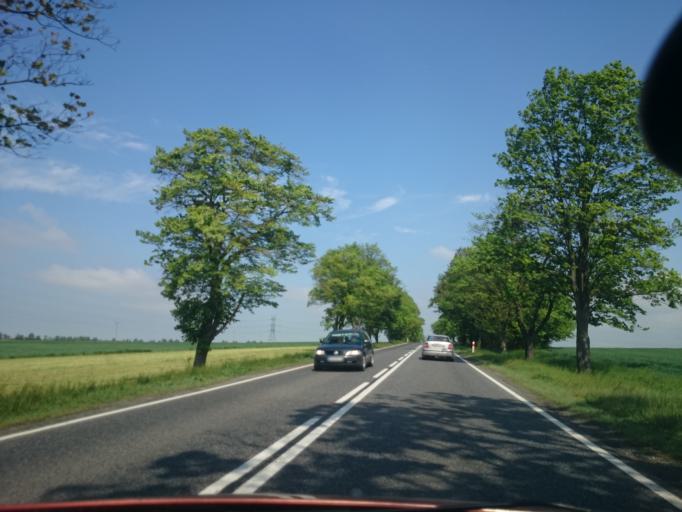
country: PL
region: Opole Voivodeship
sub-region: Powiat opolski
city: Dabrowa
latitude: 50.7097
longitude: 17.7777
